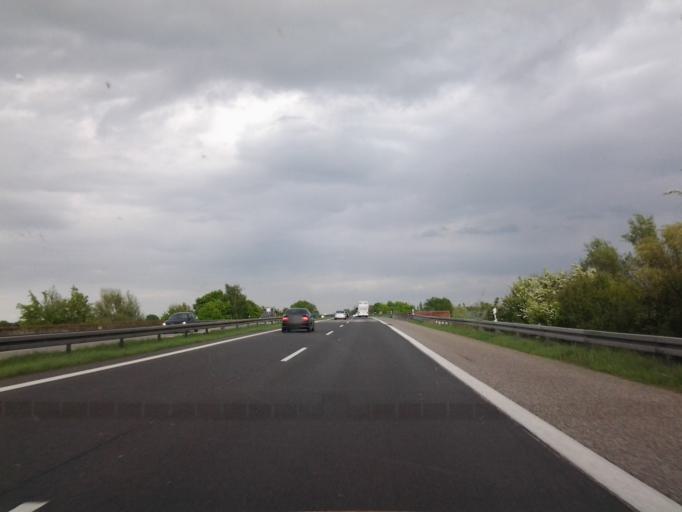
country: DE
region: Brandenburg
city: Velten
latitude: 52.7057
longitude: 13.1394
